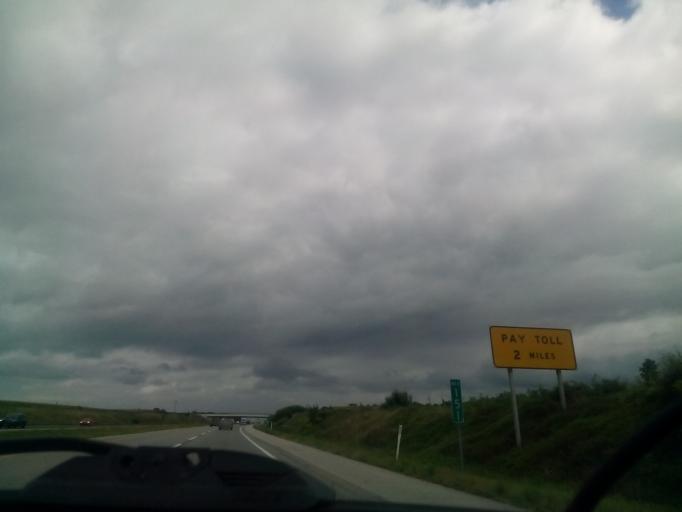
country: US
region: Indiana
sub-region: Steuben County
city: Fremont
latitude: 41.6842
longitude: -84.8830
